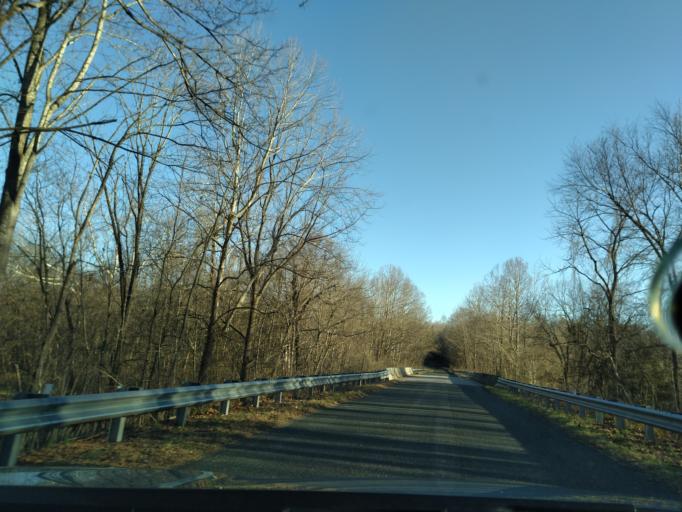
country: US
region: Virginia
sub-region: Prince Edward County
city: Hampden Sydney
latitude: 37.3526
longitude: -78.6004
